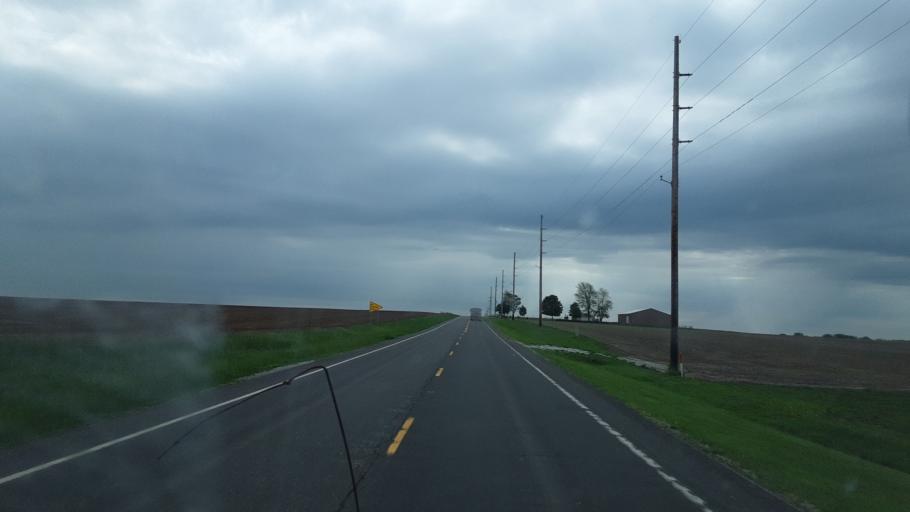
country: US
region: Illinois
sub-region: Fulton County
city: Astoria
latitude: 40.3568
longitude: -90.4101
